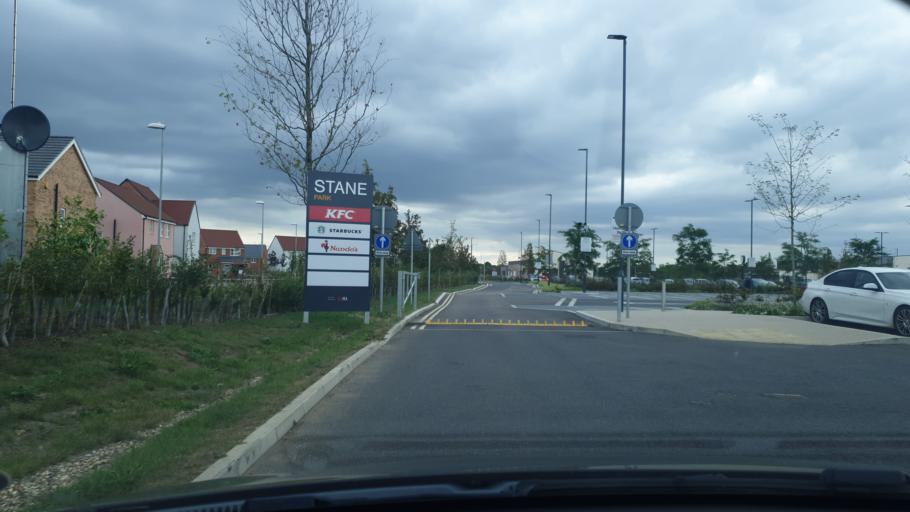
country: GB
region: England
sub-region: Essex
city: Eight Ash Green
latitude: 51.8857
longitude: 0.8258
